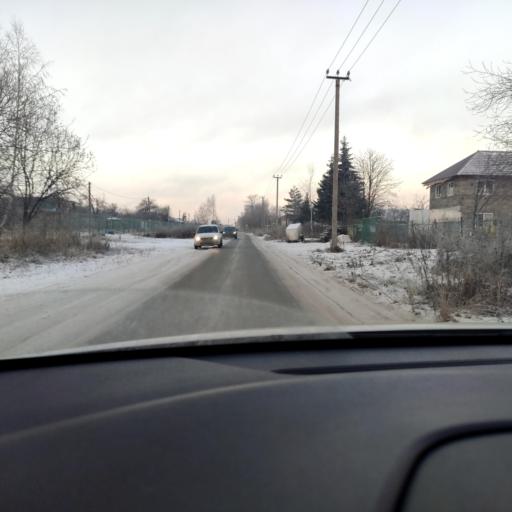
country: RU
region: Tatarstan
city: Staroye Arakchino
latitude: 55.8607
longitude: 49.0514
